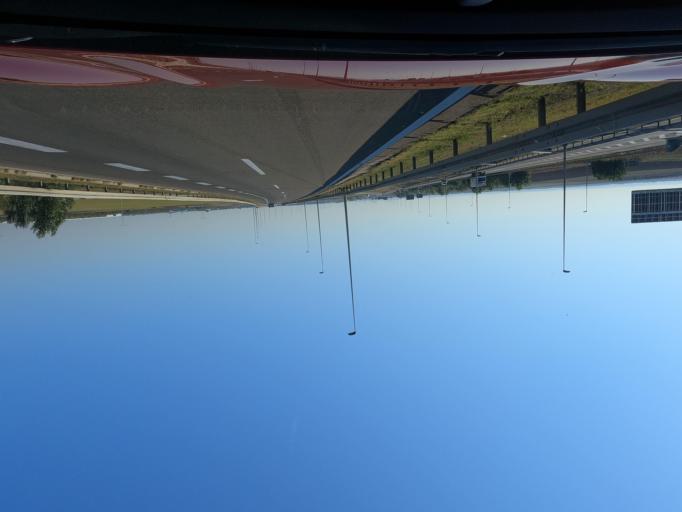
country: RS
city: Dobanovci
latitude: 44.8327
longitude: 20.2513
